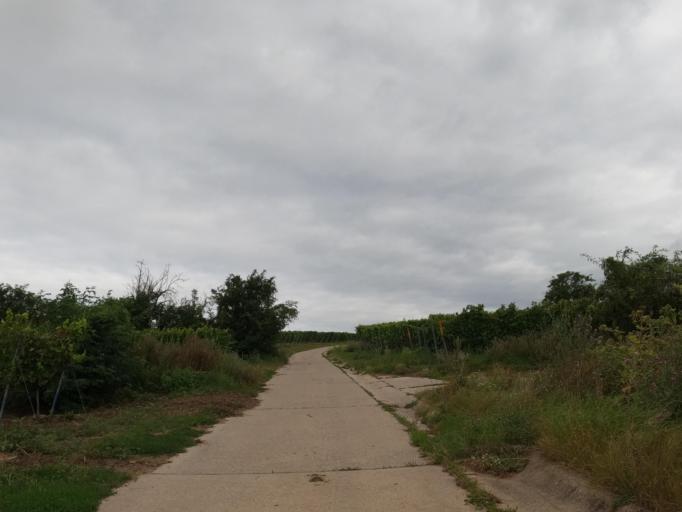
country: DE
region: Rheinland-Pfalz
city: Bissersheim
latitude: 49.5293
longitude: 8.2053
